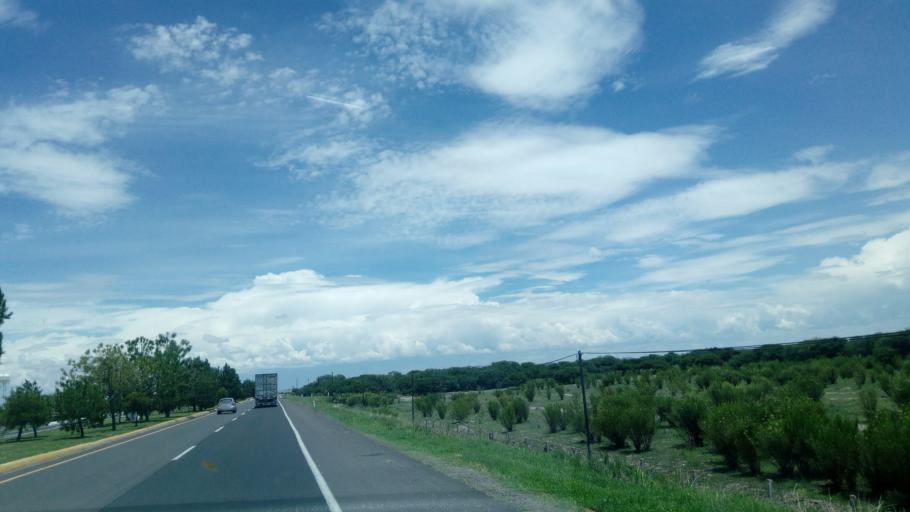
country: MX
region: Durango
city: Victoria de Durango
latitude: 24.1014
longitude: -104.5661
